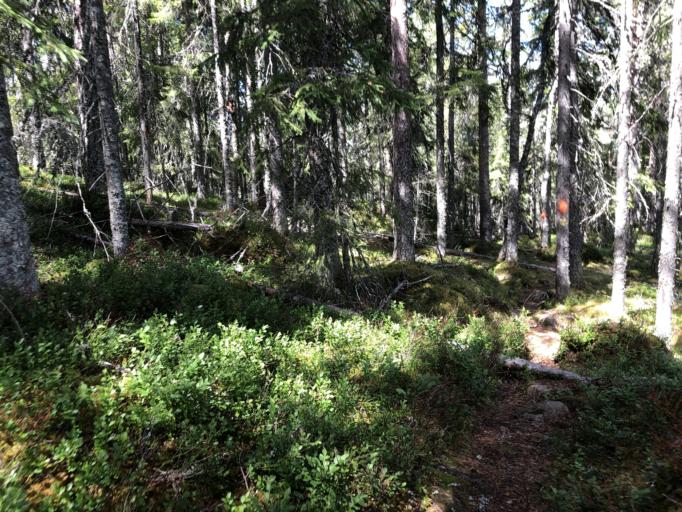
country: SE
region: Dalarna
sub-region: Vansbro Kommun
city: Jarna
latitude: 60.6660
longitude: 14.2717
